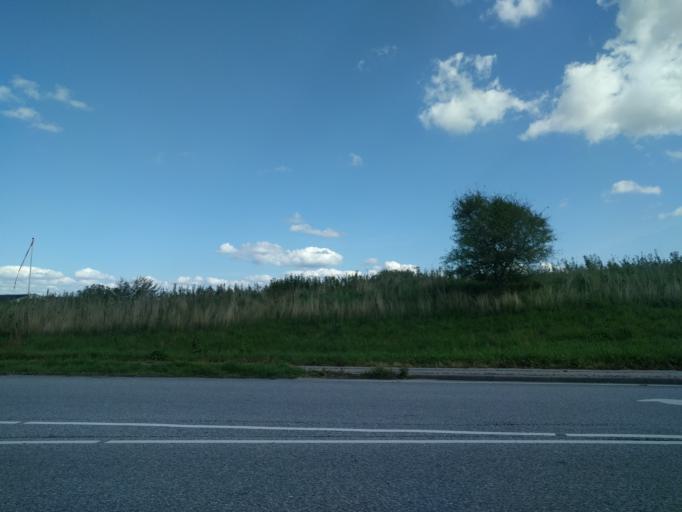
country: DK
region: Central Jutland
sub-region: Skive Kommune
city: Skive
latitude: 56.5919
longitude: 9.0281
